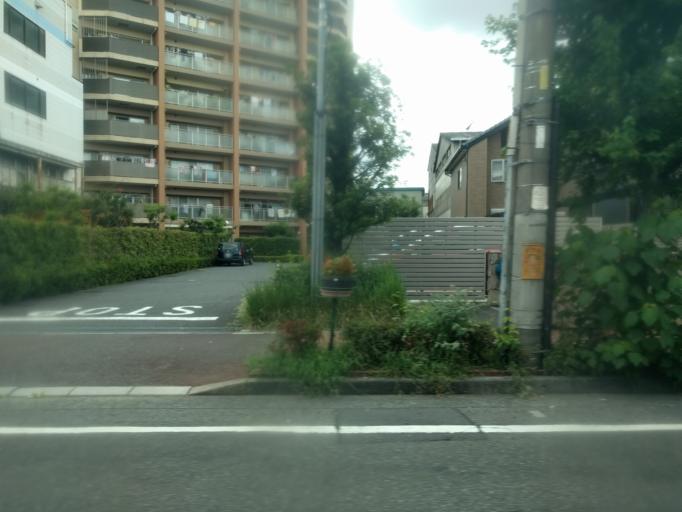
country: JP
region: Saitama
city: Kawaguchi
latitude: 35.8212
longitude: 139.7207
